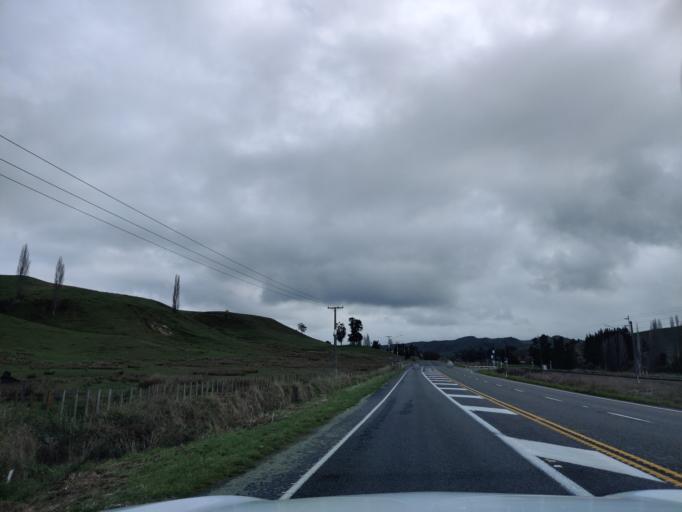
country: NZ
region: Manawatu-Wanganui
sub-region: Ruapehu District
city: Waiouru
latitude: -39.7206
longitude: 175.8407
